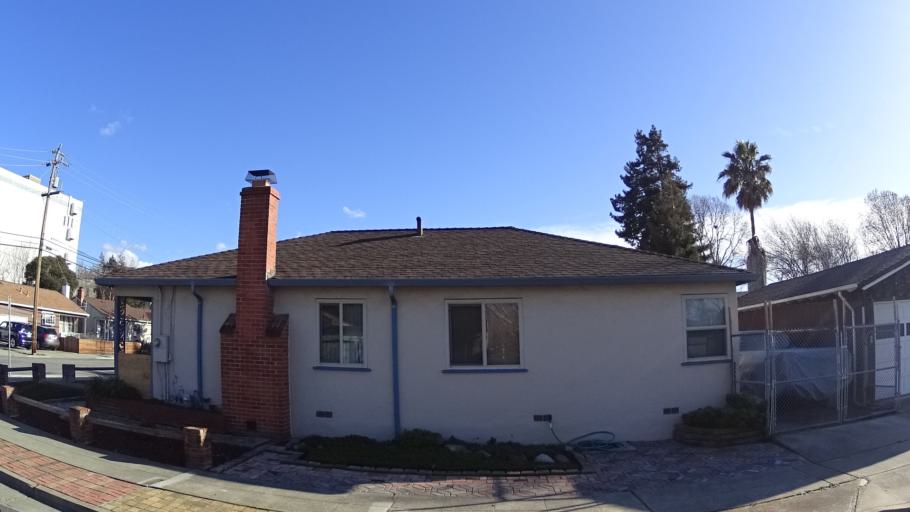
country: US
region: California
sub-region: Alameda County
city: Hayward
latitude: 37.6600
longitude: -122.0983
